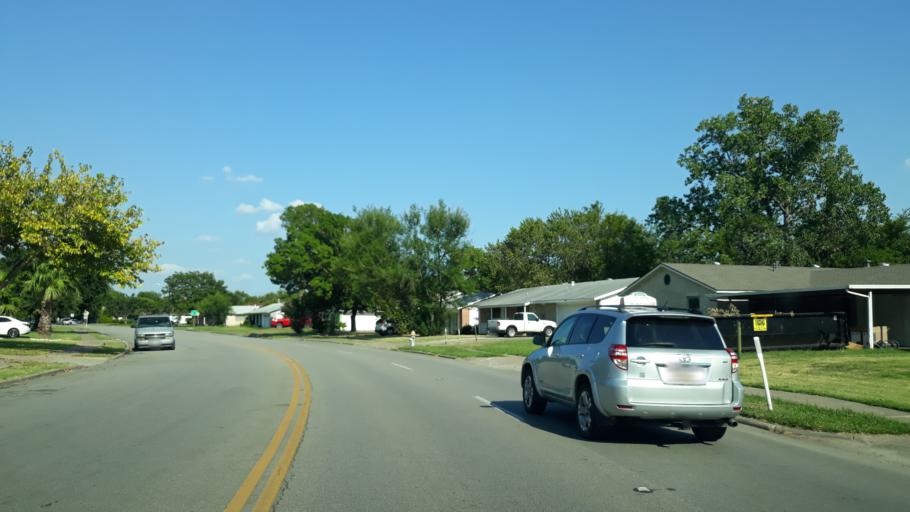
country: US
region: Texas
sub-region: Dallas County
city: Irving
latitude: 32.8414
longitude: -96.9803
